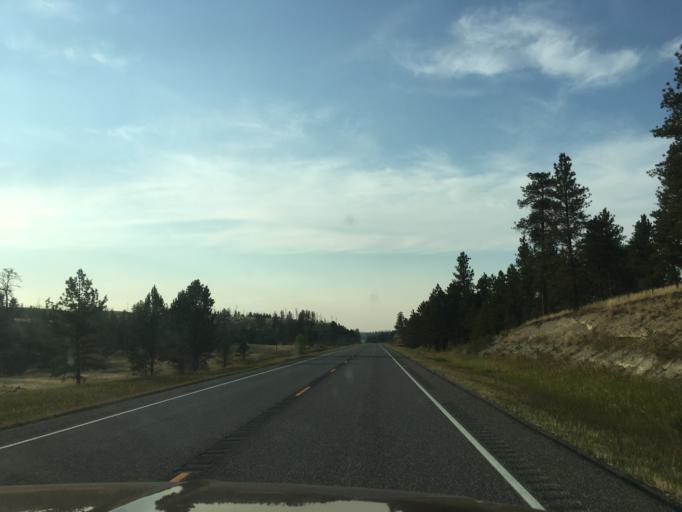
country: US
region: Montana
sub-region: Musselshell County
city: Roundup
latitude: 46.2730
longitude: -108.4724
